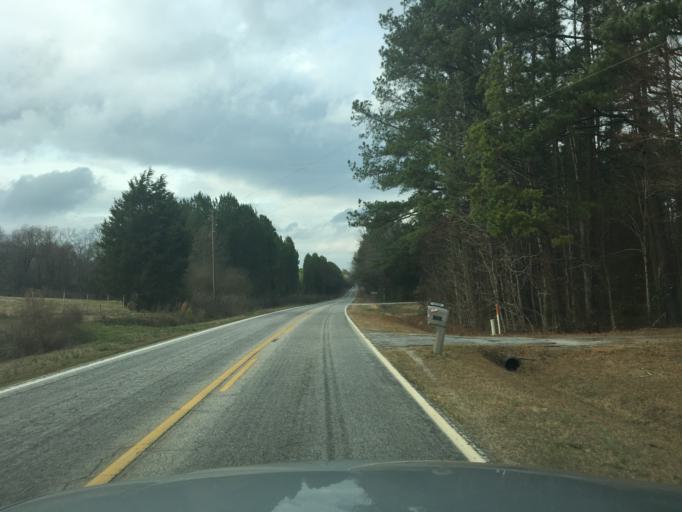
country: US
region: South Carolina
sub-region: Abbeville County
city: Abbeville
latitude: 34.2494
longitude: -82.4144
